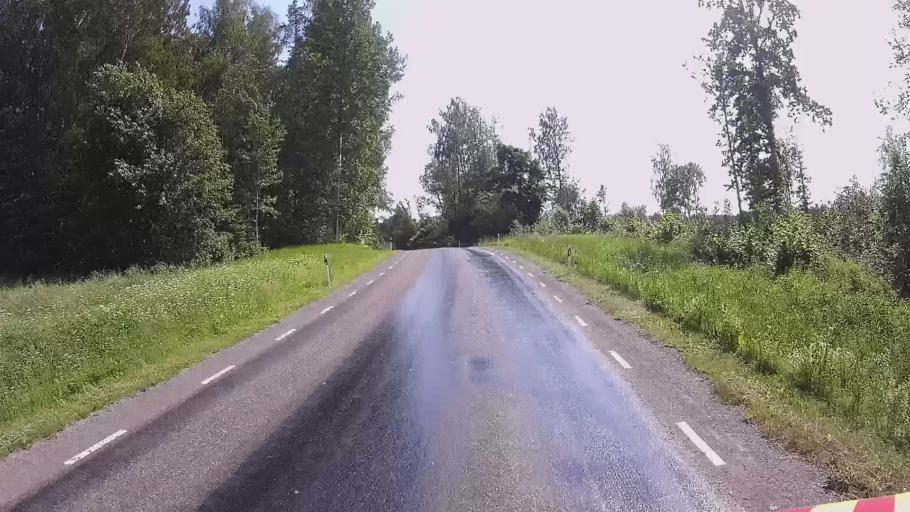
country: EE
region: Viljandimaa
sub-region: Karksi vald
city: Karksi-Nuia
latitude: 58.0419
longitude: 25.5458
